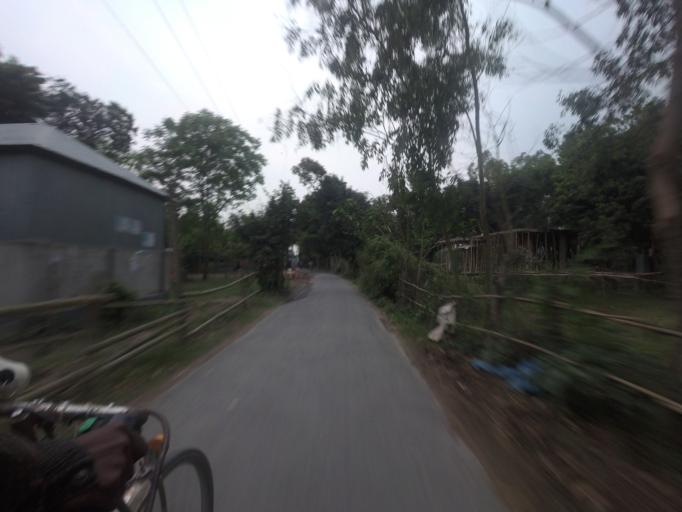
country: BD
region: Rajshahi
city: Sirajganj
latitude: 24.3172
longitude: 89.6592
